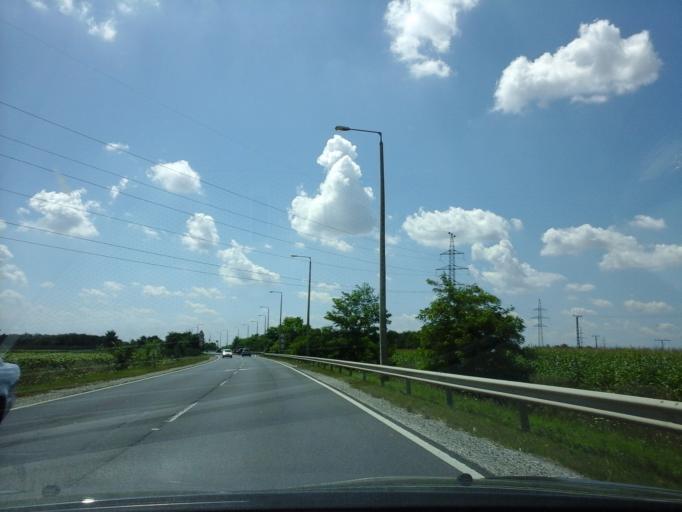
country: HU
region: Hajdu-Bihar
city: Ebes
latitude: 47.4625
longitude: 21.4497
